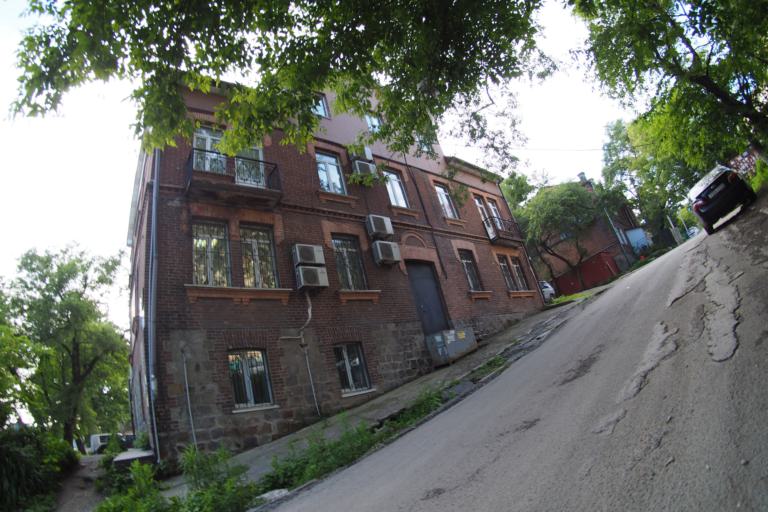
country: RU
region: Primorskiy
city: Vladivostok
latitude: 43.1125
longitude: 131.9213
